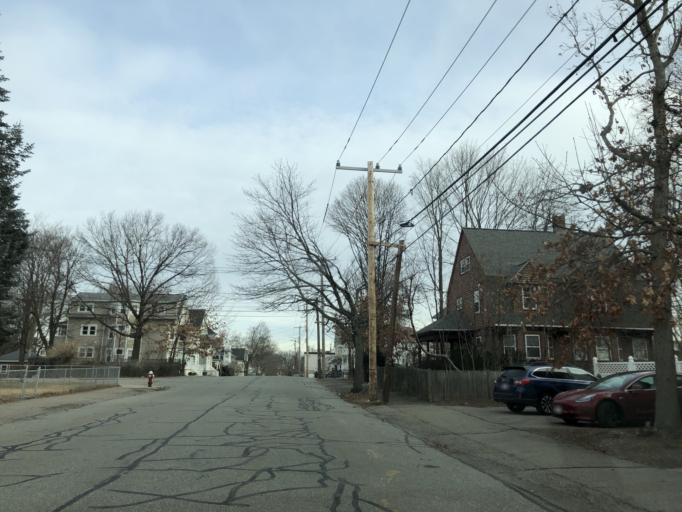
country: US
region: Massachusetts
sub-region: Middlesex County
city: Watertown
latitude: 42.3657
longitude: -71.1642
